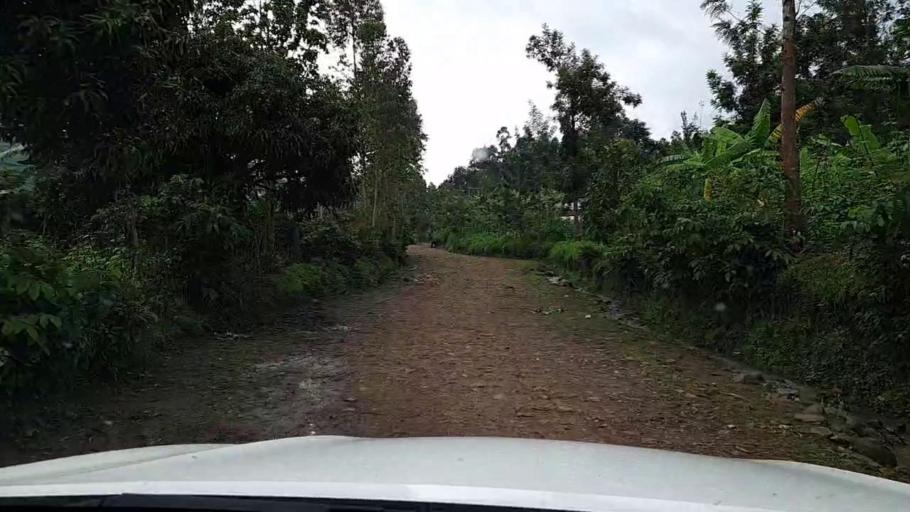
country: RW
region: Western Province
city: Cyangugu
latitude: -2.5422
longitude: 29.0391
